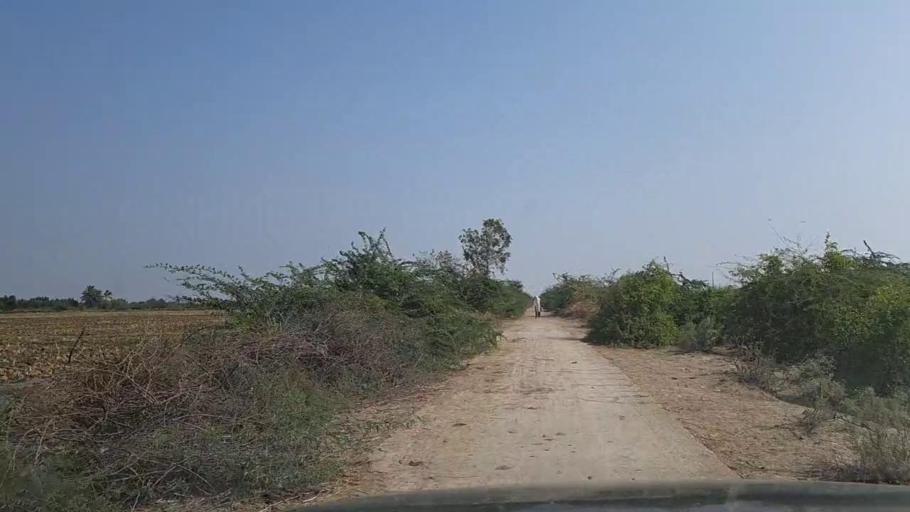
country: PK
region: Sindh
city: Gharo
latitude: 24.7394
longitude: 67.6818
